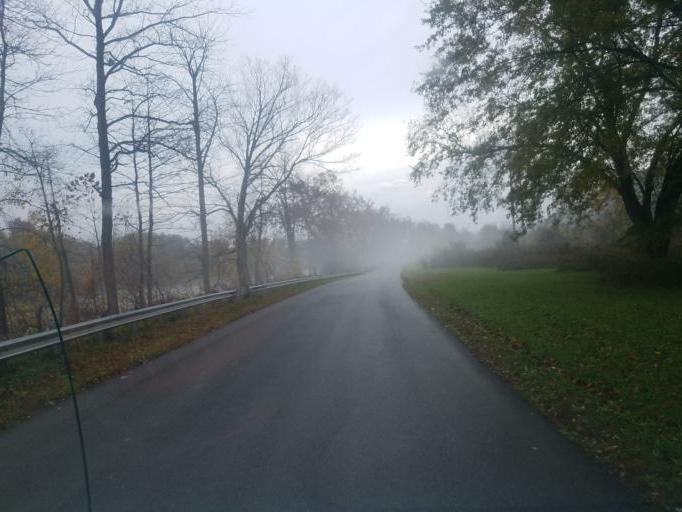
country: US
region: Ohio
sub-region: Morgan County
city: McConnelsville
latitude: 39.5369
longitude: -81.7818
